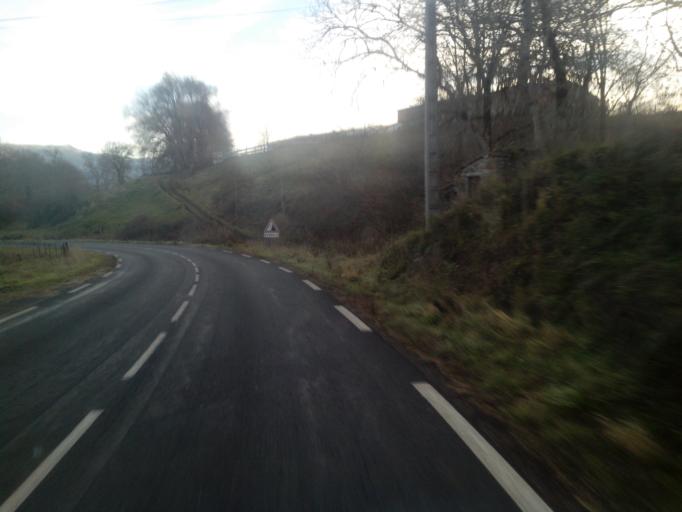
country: FR
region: Auvergne
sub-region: Departement du Cantal
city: Riom-es-Montagnes
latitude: 45.2501
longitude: 2.7056
